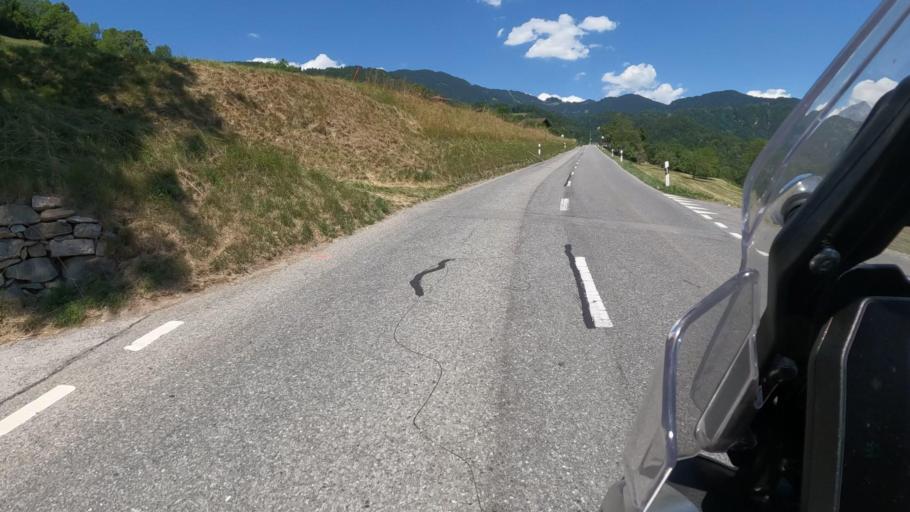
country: CH
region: Vaud
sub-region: Aigle District
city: Bex
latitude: 46.2830
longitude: 7.0248
